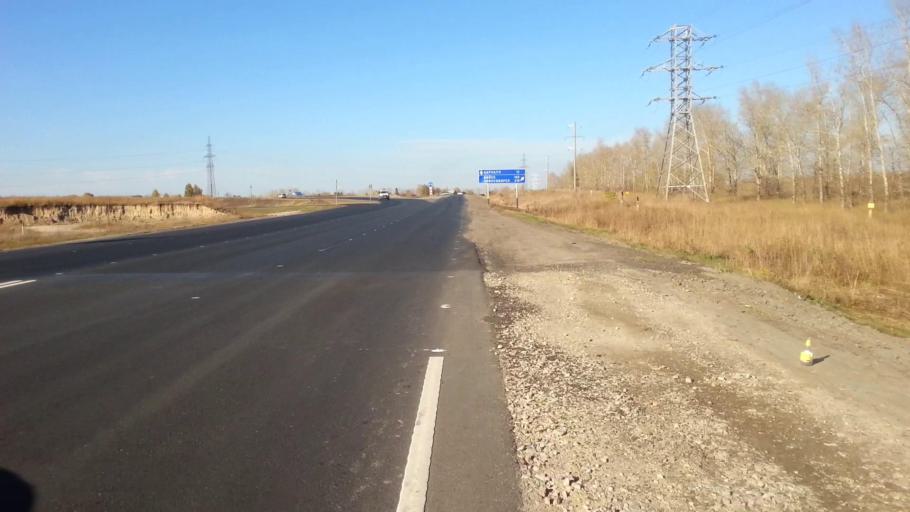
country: RU
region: Altai Krai
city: Sannikovo
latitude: 53.3376
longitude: 83.9387
